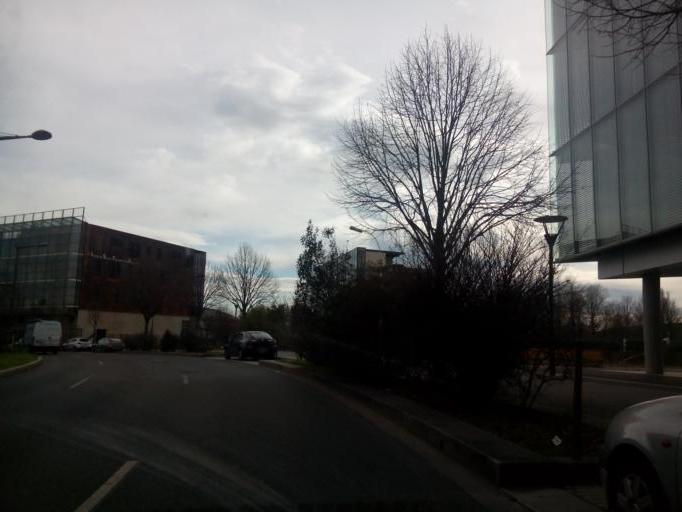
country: FR
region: Rhone-Alpes
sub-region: Departement du Rhone
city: La Mulatiere
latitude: 45.7270
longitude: 4.8246
